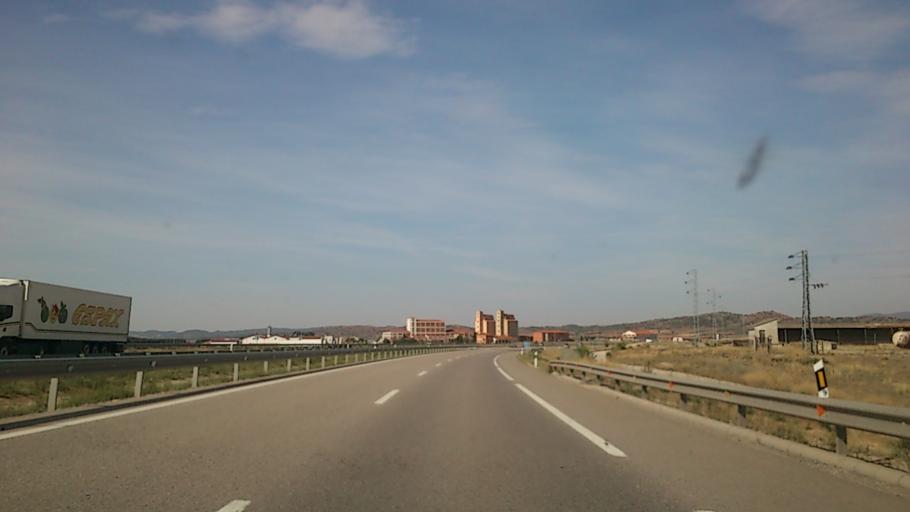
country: ES
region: Aragon
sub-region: Provincia de Teruel
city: Calamocha
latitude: 40.8976
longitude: -1.3030
